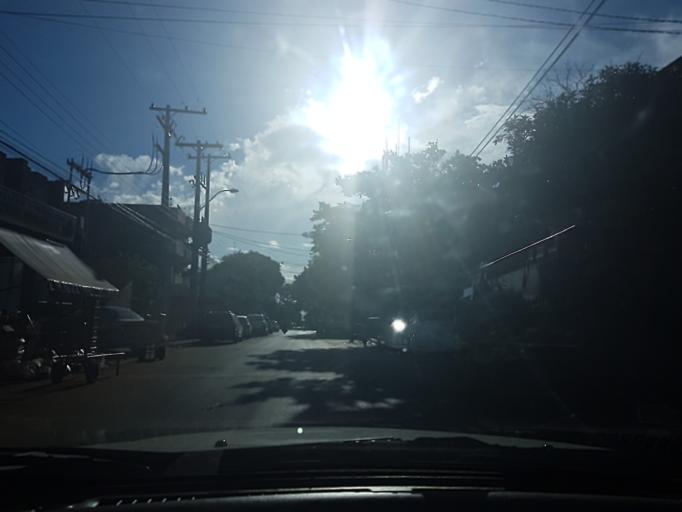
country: PY
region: Central
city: San Lorenzo
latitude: -25.2708
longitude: -57.4899
